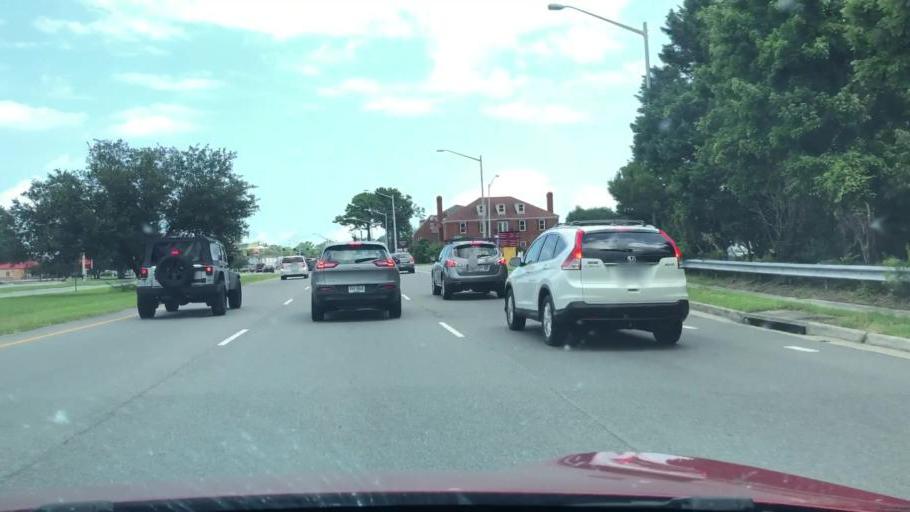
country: US
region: Virginia
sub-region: City of Chesapeake
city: Chesapeake
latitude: 36.8604
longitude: -76.1327
